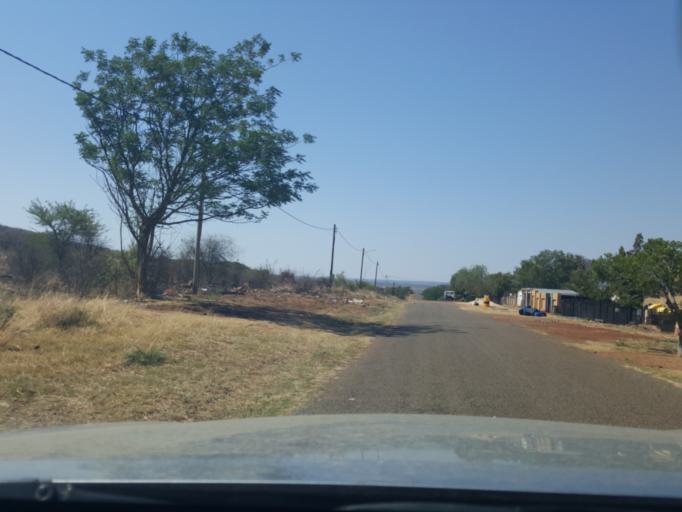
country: ZA
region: North-West
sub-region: Ngaka Modiri Molema District Municipality
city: Zeerust
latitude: -25.5251
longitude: 26.0799
